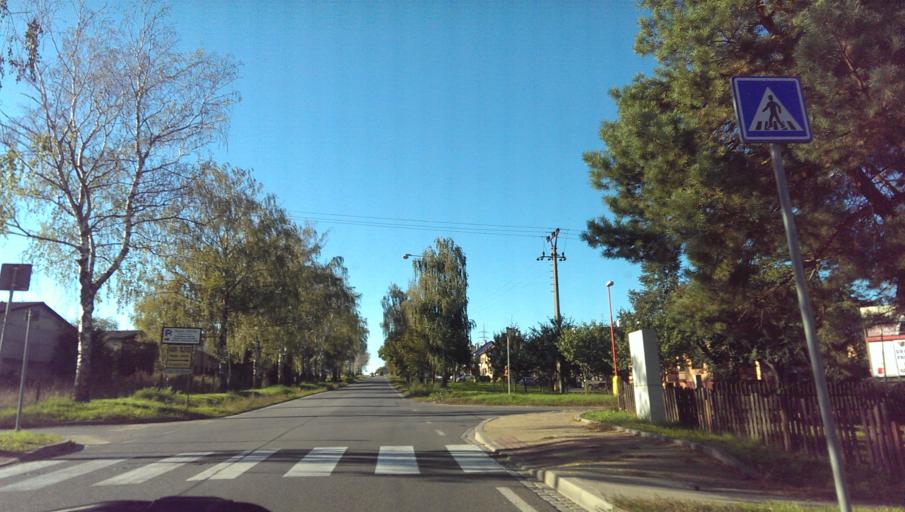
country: CZ
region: Zlin
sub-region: Okres Uherske Hradiste
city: Stare Mesto
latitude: 49.0825
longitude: 17.4380
